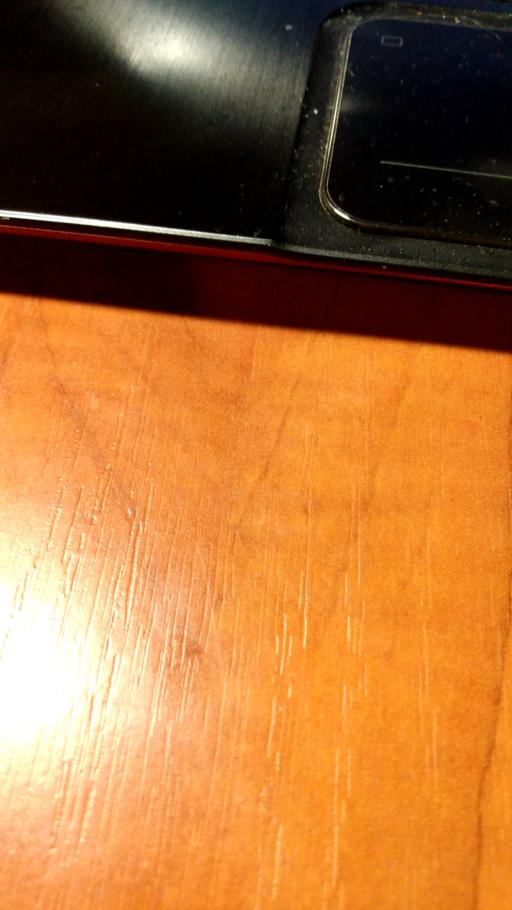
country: RU
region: Novgorod
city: Marevo
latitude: 57.3327
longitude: 32.0238
